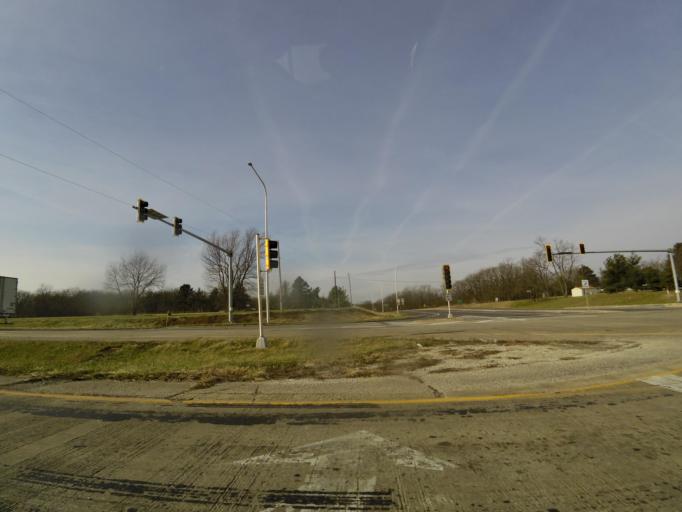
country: US
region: Illinois
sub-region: De Witt County
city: Clinton
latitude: 40.1534
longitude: -88.9848
